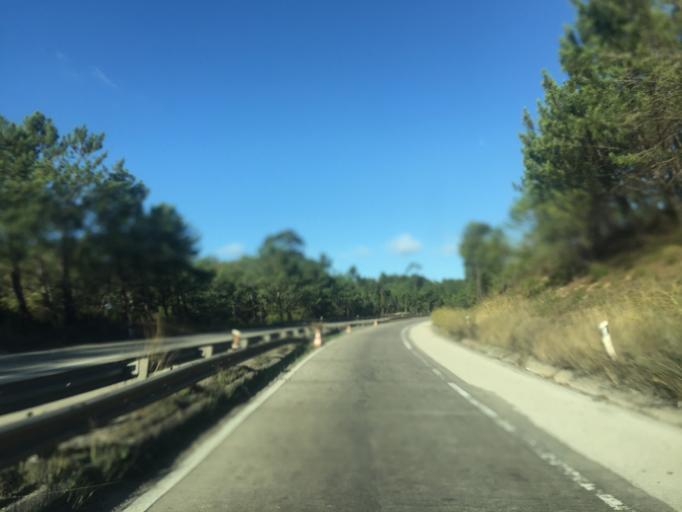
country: PT
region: Santarem
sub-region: Rio Maior
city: Rio Maior
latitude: 39.3229
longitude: -8.9498
